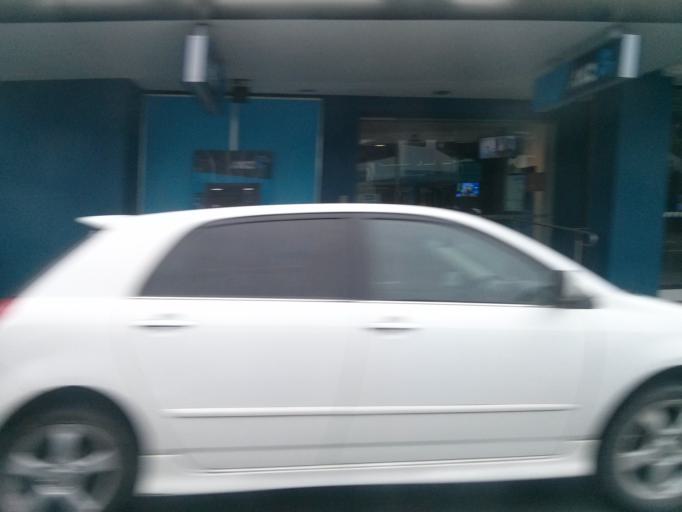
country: NZ
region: Canterbury
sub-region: Christchurch City
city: Christchurch
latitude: -43.4960
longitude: 172.6083
